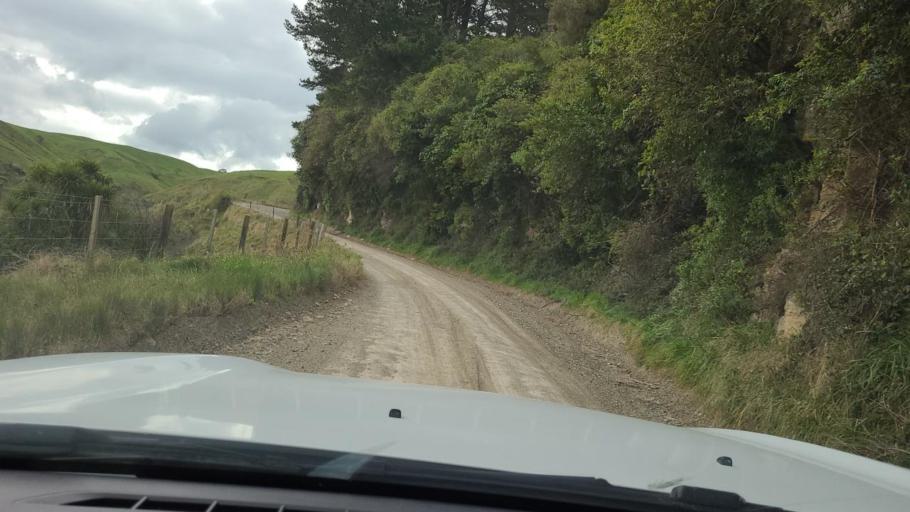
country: NZ
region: Hawke's Bay
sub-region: Napier City
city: Napier
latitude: -39.2699
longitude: 176.8381
